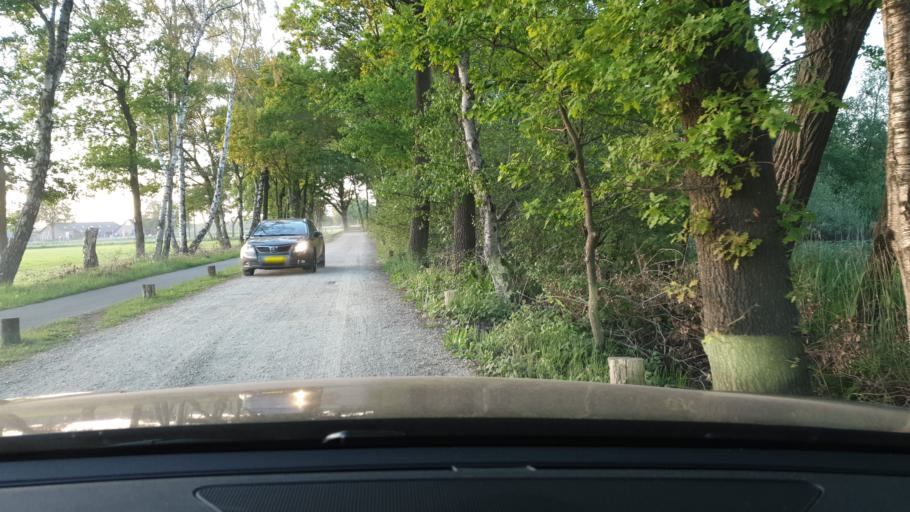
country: NL
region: North Brabant
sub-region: Gemeente Valkenswaard
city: Valkenswaard
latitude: 51.3343
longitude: 5.4436
